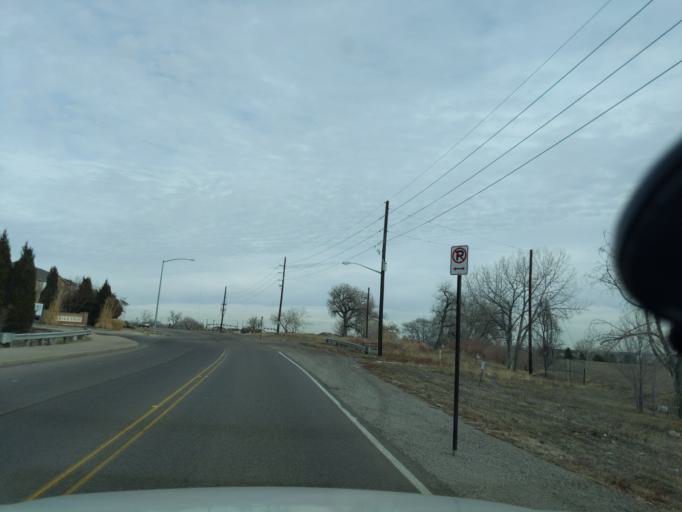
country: US
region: Colorado
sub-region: Adams County
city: Thornton
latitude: 39.8677
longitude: -104.9441
